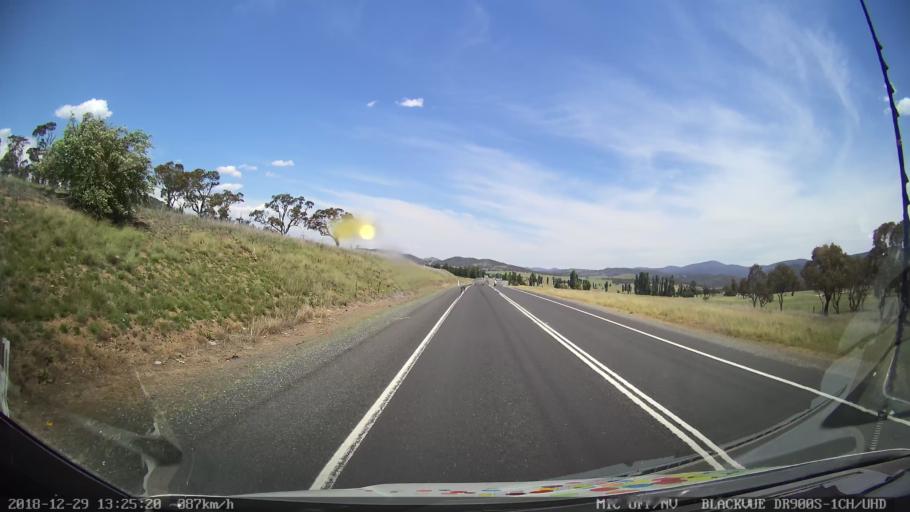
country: AU
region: New South Wales
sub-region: Cooma-Monaro
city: Cooma
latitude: -35.8412
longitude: 149.1615
